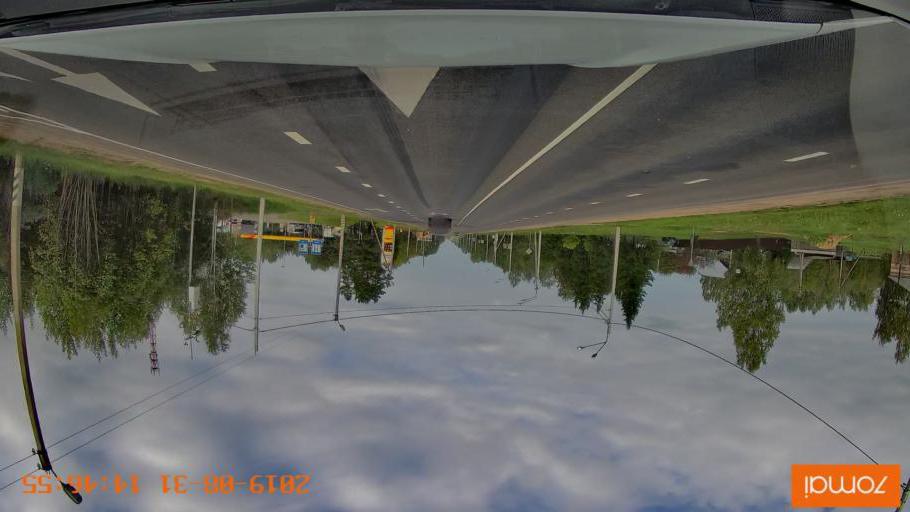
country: RU
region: Kaluga
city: Betlitsa
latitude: 54.2366
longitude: 33.7184
